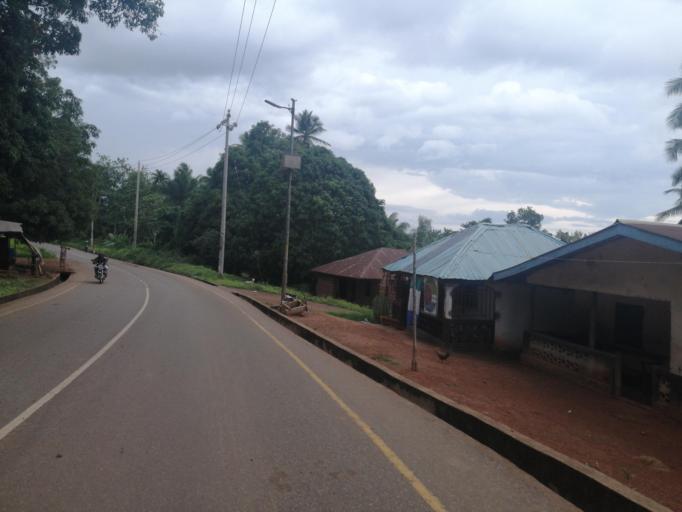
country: SL
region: Northern Province
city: Port Loko
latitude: 8.7579
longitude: -12.7871
